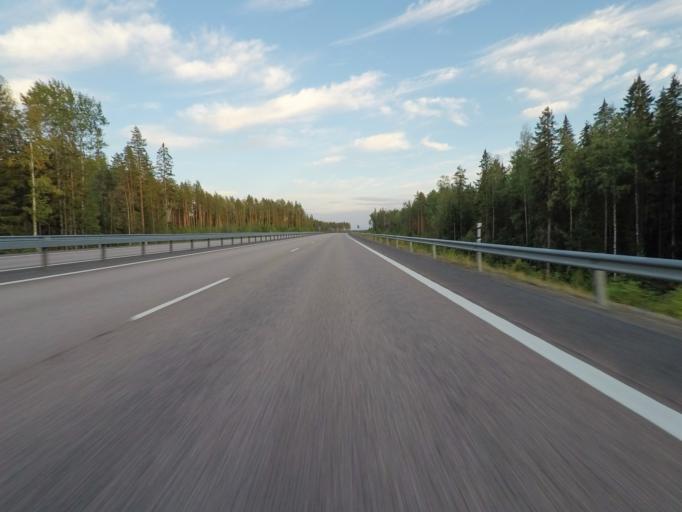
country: FI
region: Central Finland
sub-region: Jyvaeskylae
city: Toivakka
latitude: 62.1156
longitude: 25.9659
